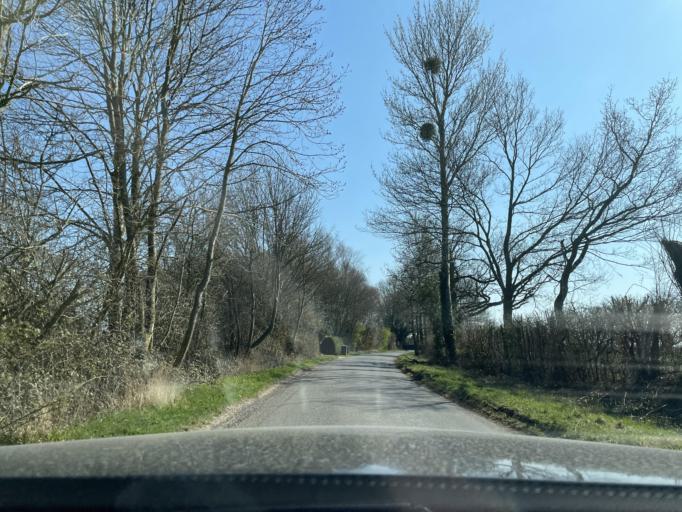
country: GB
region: England
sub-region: Norfolk
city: Hingham
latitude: 52.6190
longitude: 0.9846
